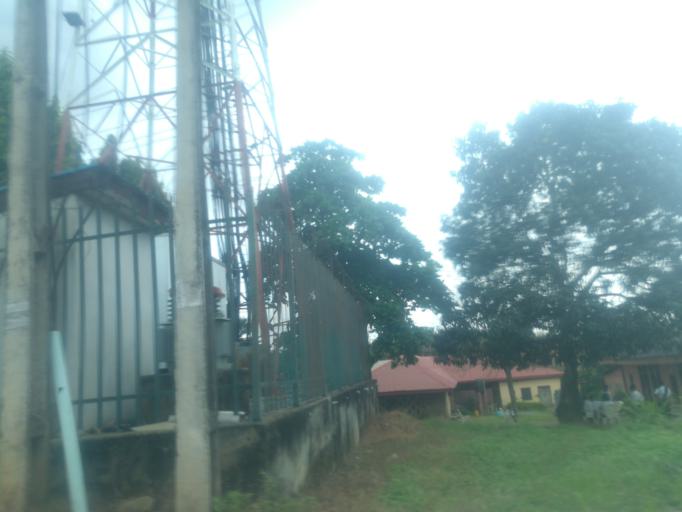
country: NG
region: Oyo
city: Ibadan
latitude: 7.4285
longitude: 3.8957
